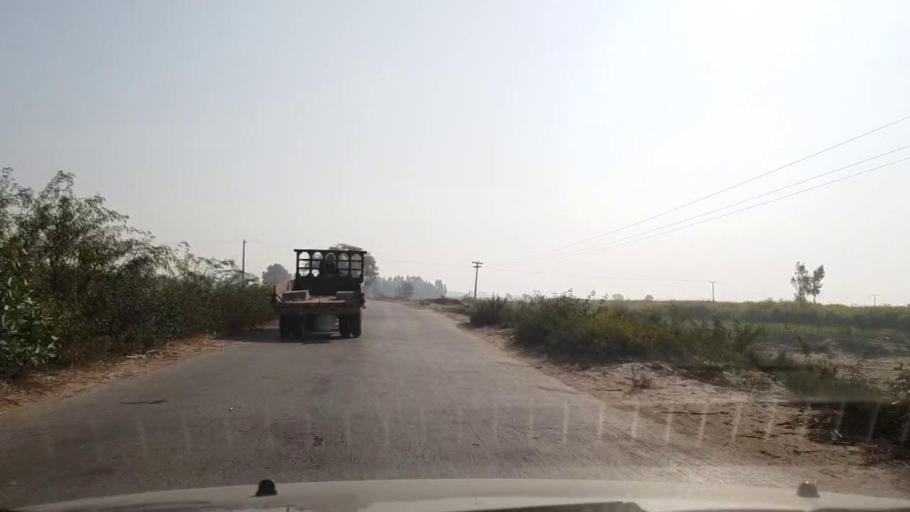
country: PK
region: Sindh
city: Matiari
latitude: 25.5654
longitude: 68.5186
